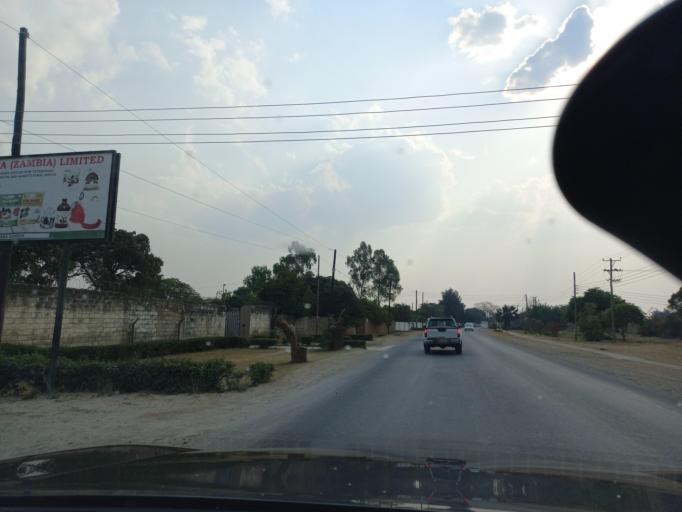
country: ZM
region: Lusaka
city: Lusaka
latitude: -15.4635
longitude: 28.2422
